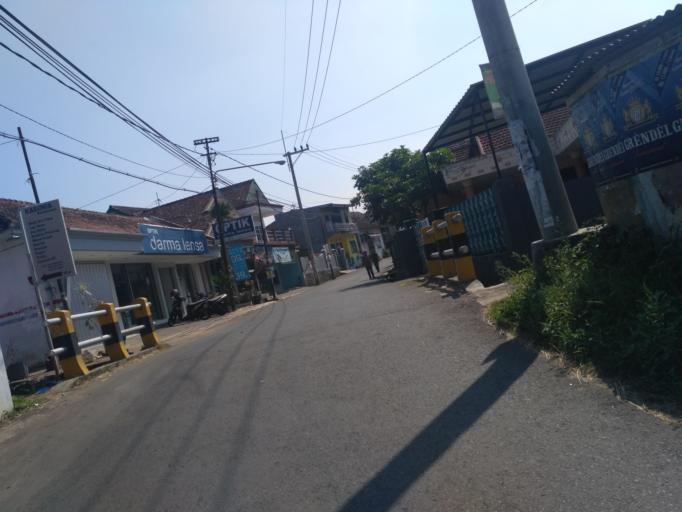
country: ID
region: East Java
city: Batu
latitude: -7.9039
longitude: 112.5813
